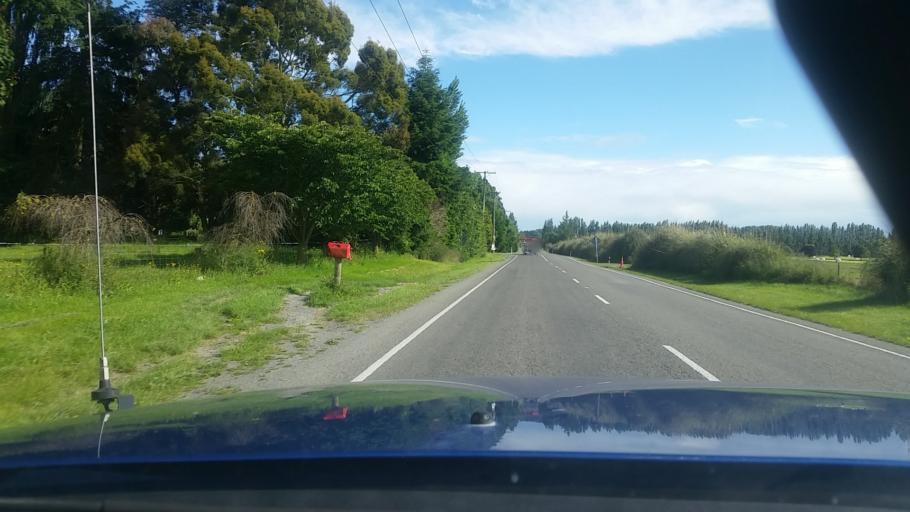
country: NZ
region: Canterbury
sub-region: Ashburton District
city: Ashburton
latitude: -43.8747
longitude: 171.7276
